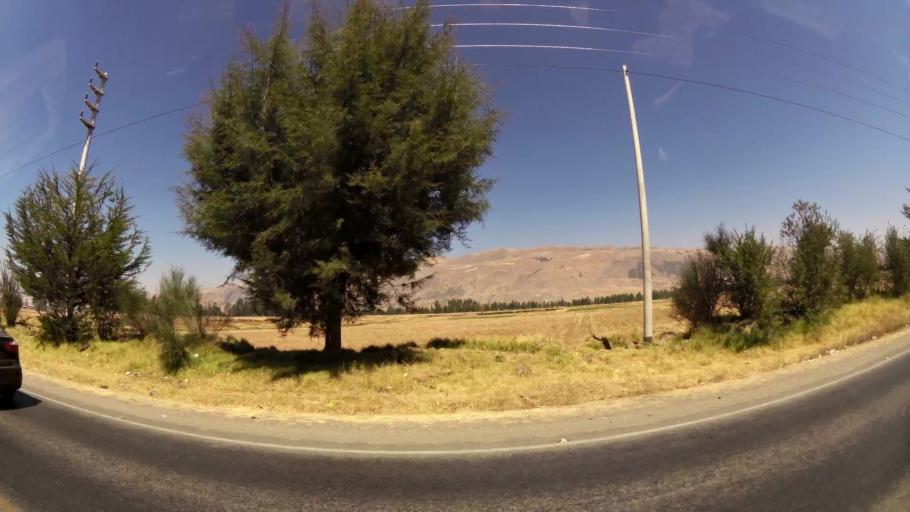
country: PE
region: Junin
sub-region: Provincia de Jauja
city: Huamali
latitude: -11.8246
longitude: -75.4094
